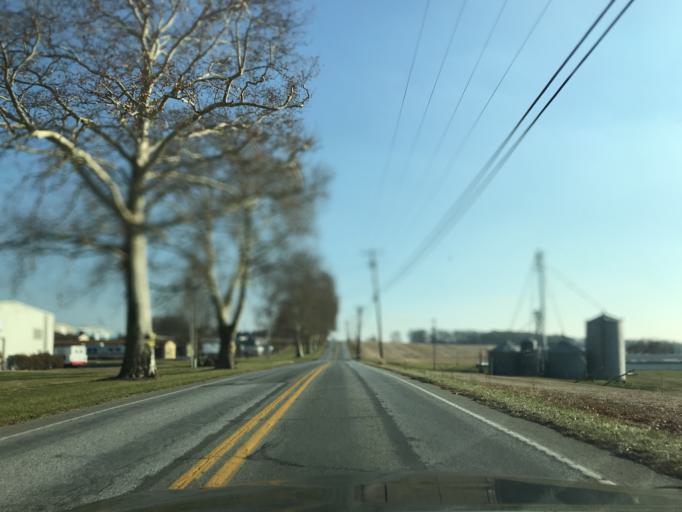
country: US
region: Pennsylvania
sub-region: York County
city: Loganville
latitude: 39.8152
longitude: -76.6880
